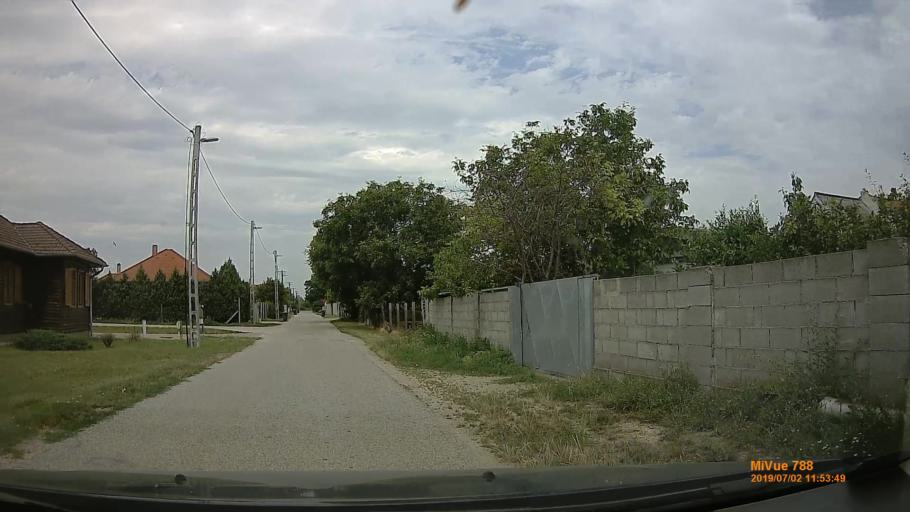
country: HU
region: Gyor-Moson-Sopron
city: Janossomorja
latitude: 47.8450
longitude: 17.1716
